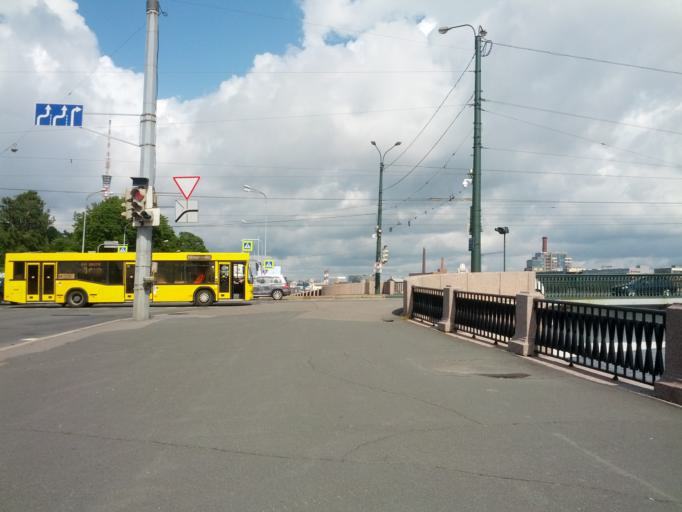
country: RU
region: Leningrad
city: Sampsonievskiy
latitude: 59.9672
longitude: 30.3331
